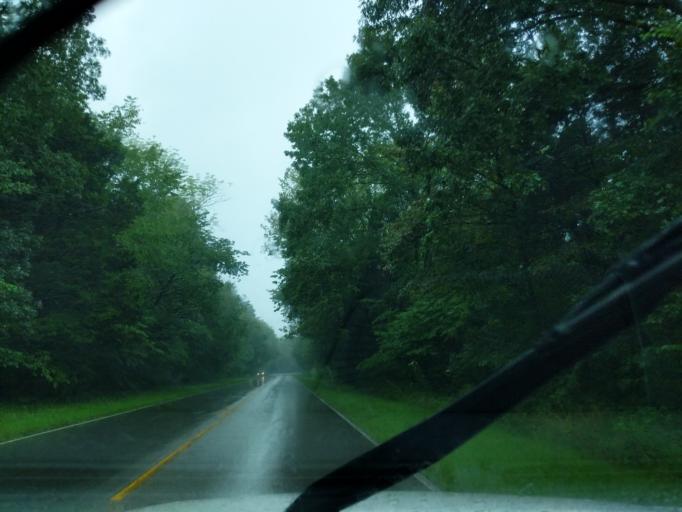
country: US
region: Kentucky
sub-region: Barren County
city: Cave City
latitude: 37.1391
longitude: -86.0792
